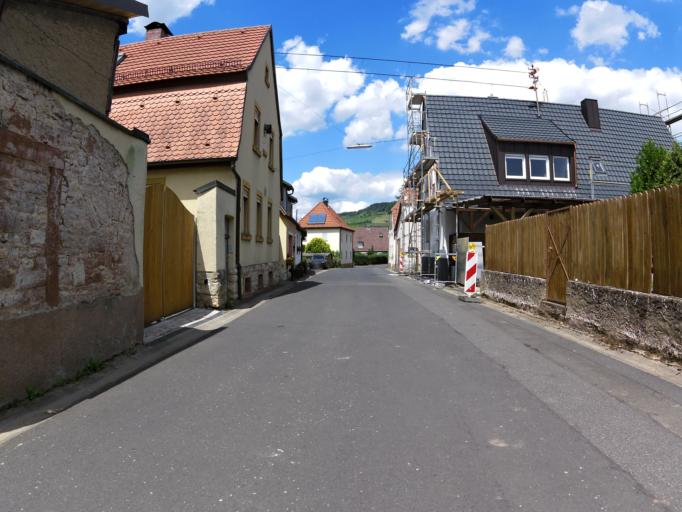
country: DE
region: Bavaria
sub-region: Regierungsbezirk Unterfranken
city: Thungersheim
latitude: 49.8804
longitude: 9.8437
